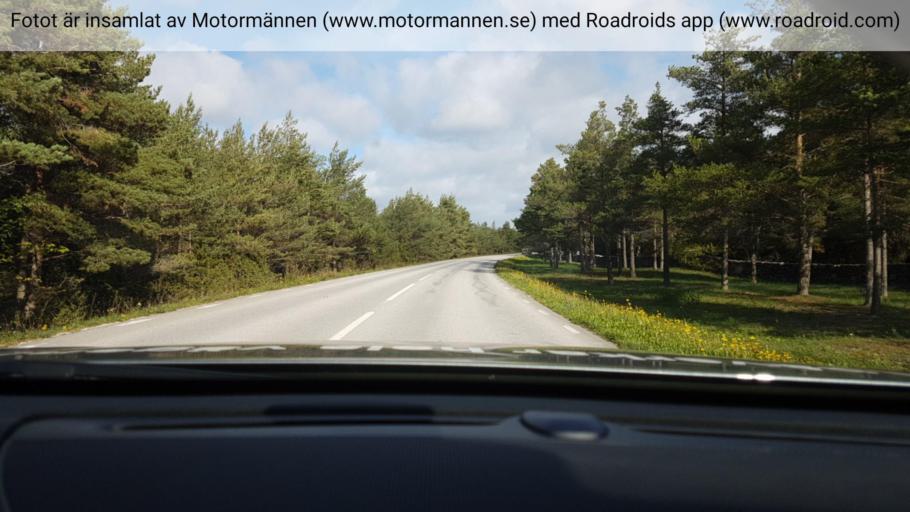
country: SE
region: Gotland
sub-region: Gotland
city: Slite
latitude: 57.8743
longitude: 19.0852
